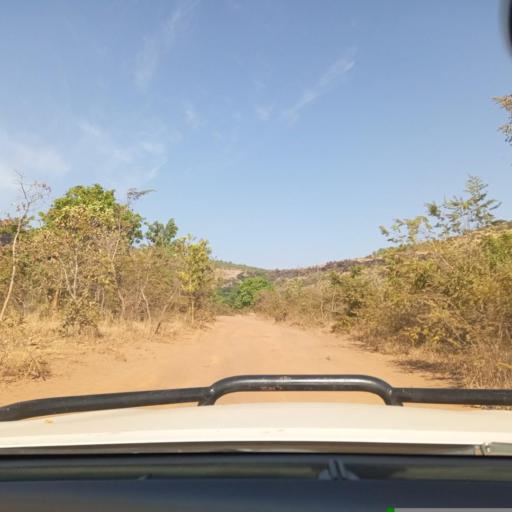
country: ML
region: Bamako
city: Bamako
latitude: 12.5585
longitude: -8.1513
